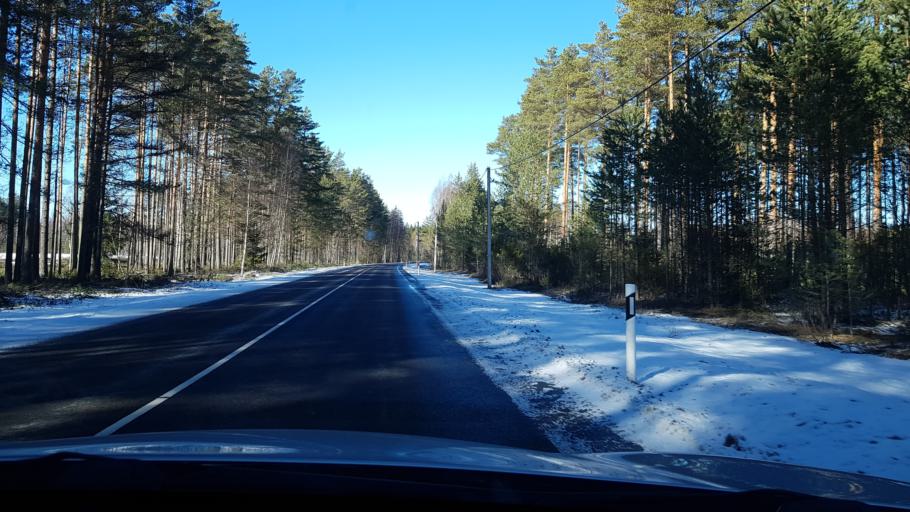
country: EE
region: Polvamaa
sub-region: Raepina vald
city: Rapina
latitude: 57.9789
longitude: 27.5706
